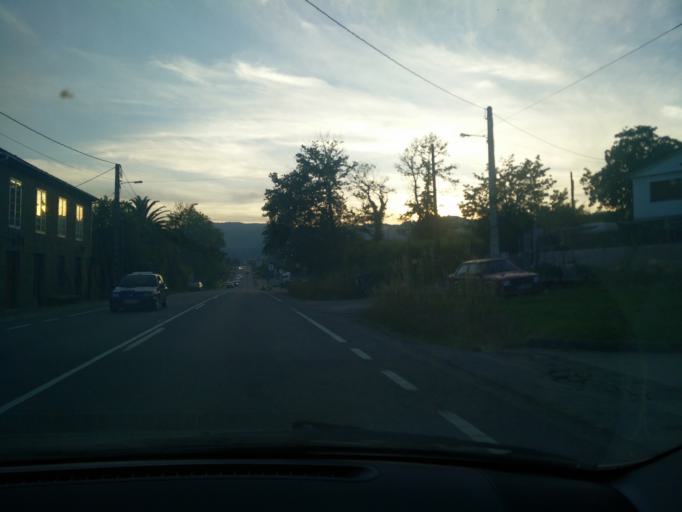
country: ES
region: Galicia
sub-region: Provincia de Pontevedra
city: Ponteareas
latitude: 42.1791
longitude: -8.5423
